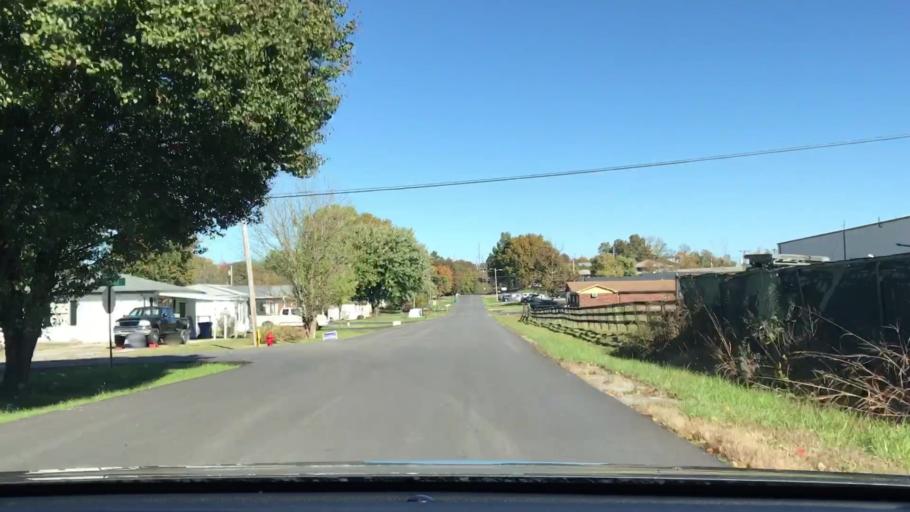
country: US
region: Kentucky
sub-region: Barren County
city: Glasgow
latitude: 36.9917
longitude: -85.9337
